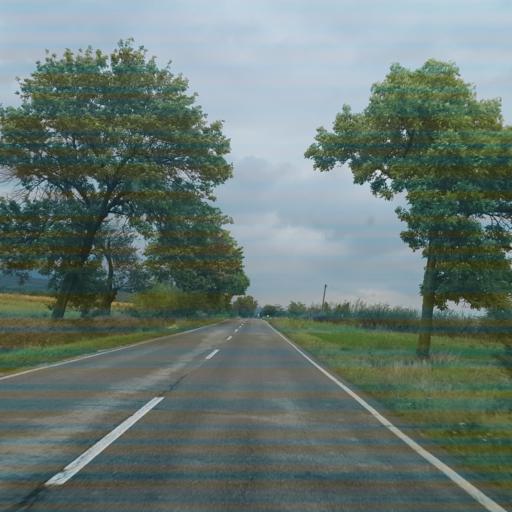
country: RS
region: Central Serbia
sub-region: Nisavski Okrug
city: Aleksinac
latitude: 43.5908
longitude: 21.6400
